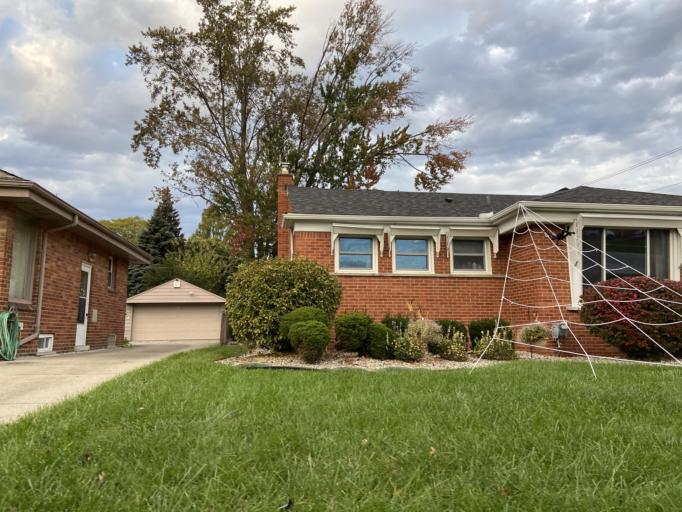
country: US
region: Michigan
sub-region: Wayne County
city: Livonia
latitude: 42.3673
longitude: -83.3235
